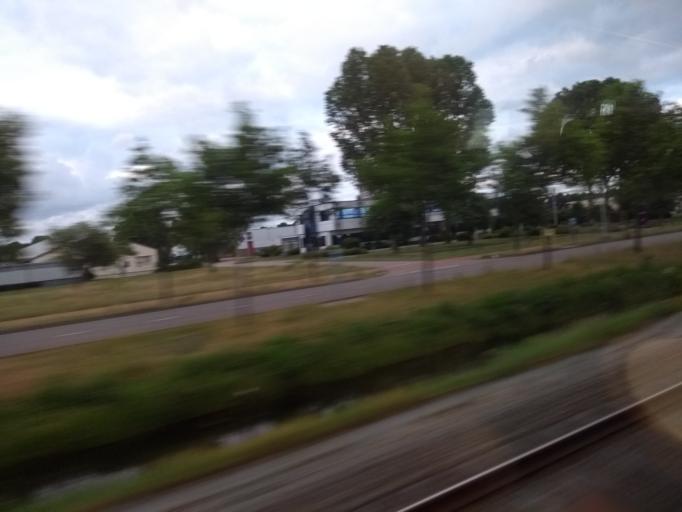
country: NL
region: Friesland
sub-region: Gemeente Heerenveen
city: Oudeschoot
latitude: 52.9317
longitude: 5.9482
